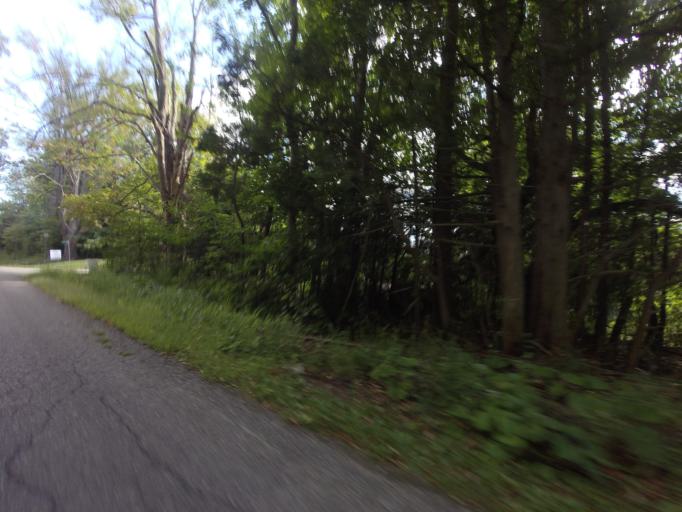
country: CA
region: Ontario
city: Orangeville
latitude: 43.8195
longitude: -79.9892
